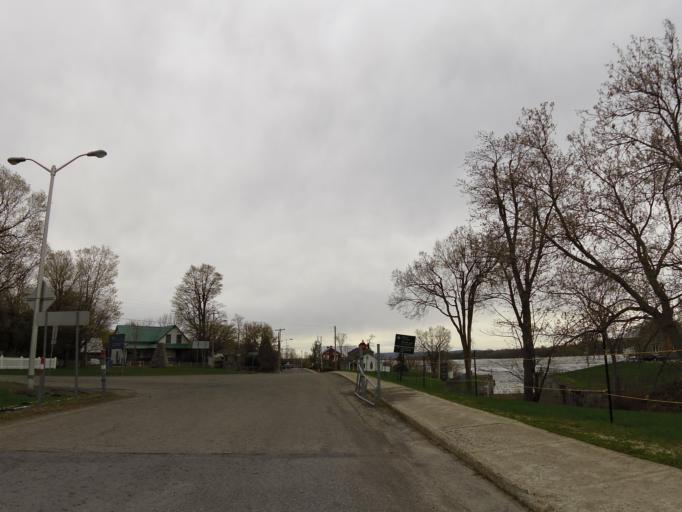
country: CA
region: Quebec
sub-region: Laurentides
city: Lachute
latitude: 45.5679
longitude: -74.3764
